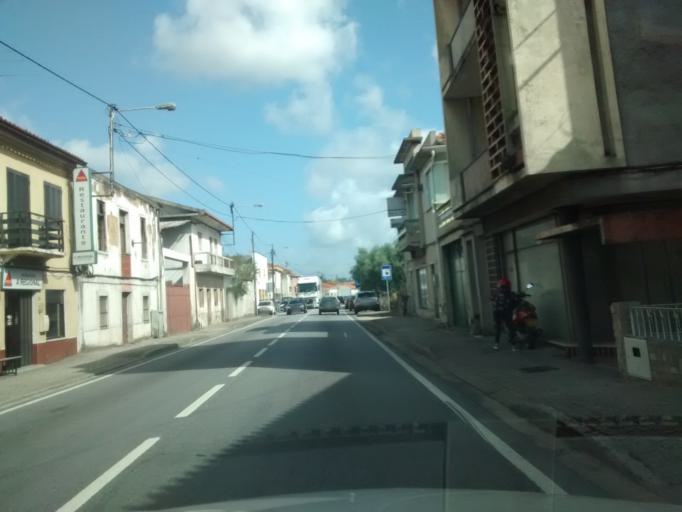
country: PT
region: Aveiro
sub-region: Anadia
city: Arcos
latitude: 40.4523
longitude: -8.4532
